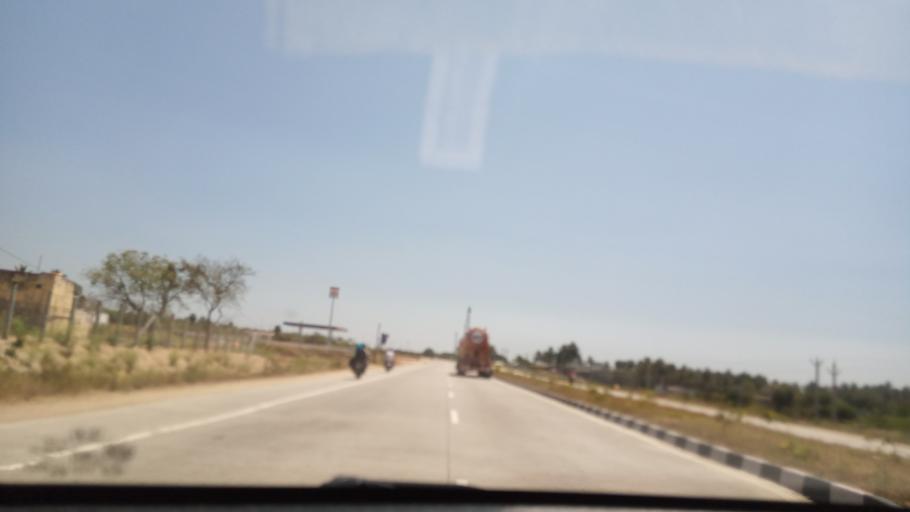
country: IN
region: Andhra Pradesh
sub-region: Chittoor
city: Chittoor
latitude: 13.2018
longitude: 78.9529
